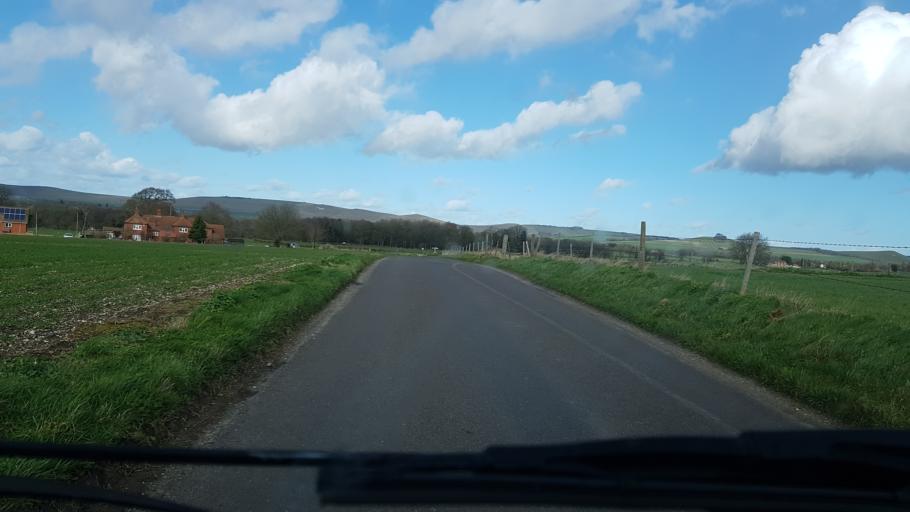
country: GB
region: England
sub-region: Wiltshire
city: Woodborough
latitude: 51.3308
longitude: -1.8641
